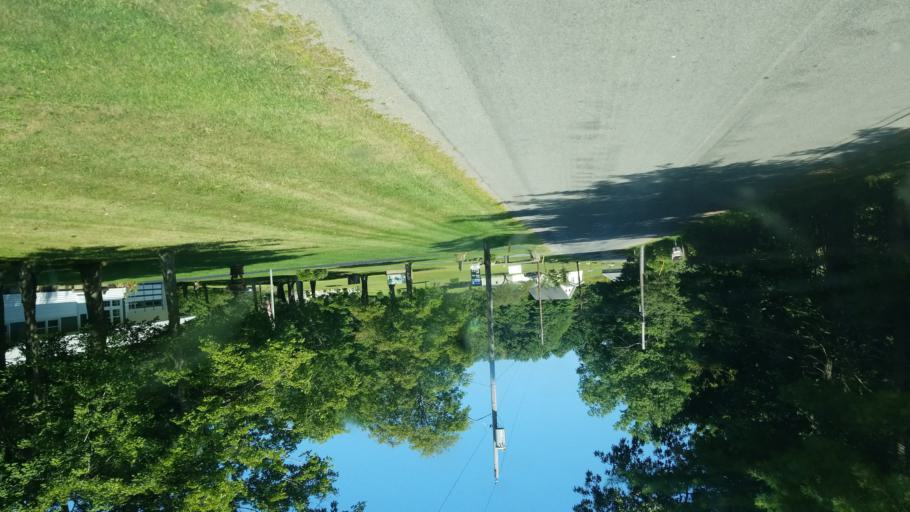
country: US
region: Pennsylvania
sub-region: Clarion County
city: Clarion
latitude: 41.1730
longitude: -79.4270
